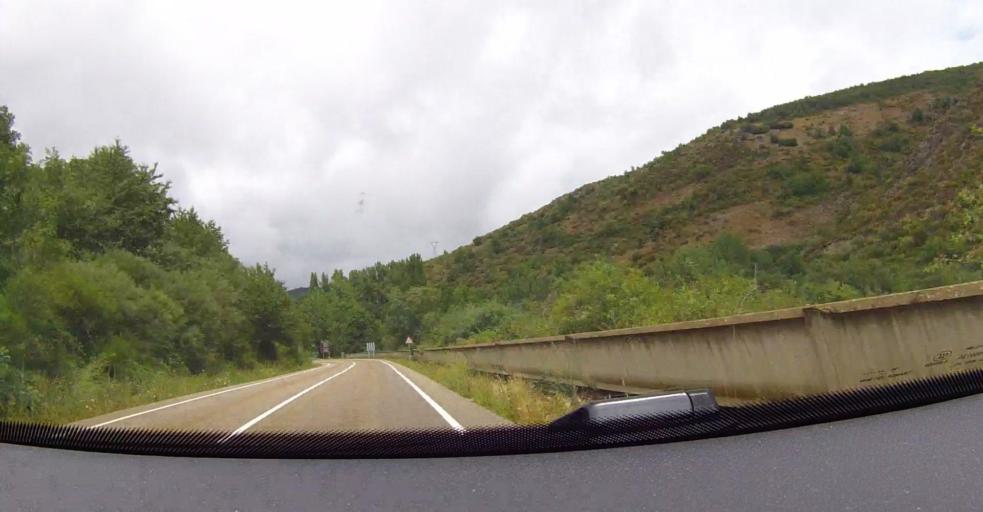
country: ES
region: Castille and Leon
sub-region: Provincia de Leon
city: Bonar
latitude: 42.8955
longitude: -5.3074
